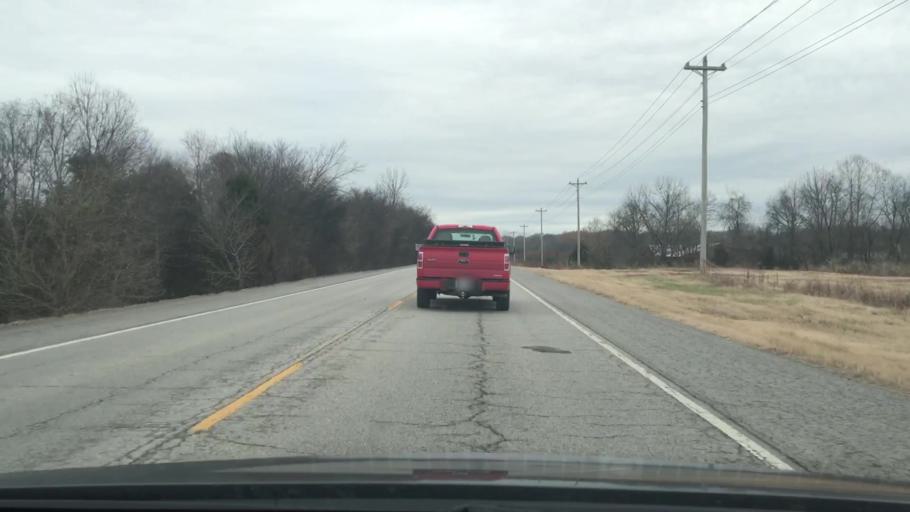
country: US
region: Tennessee
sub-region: Trousdale County
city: Hartsville
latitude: 36.3950
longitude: -86.3065
